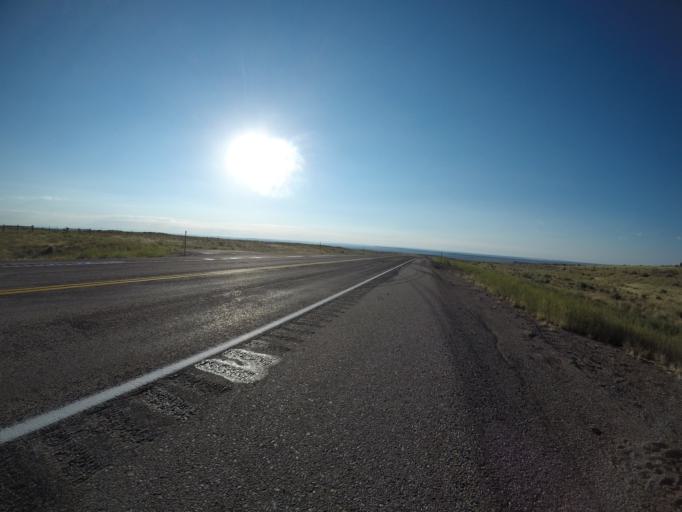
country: US
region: Wyoming
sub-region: Lincoln County
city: Kemmerer
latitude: 41.8892
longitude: -110.3941
